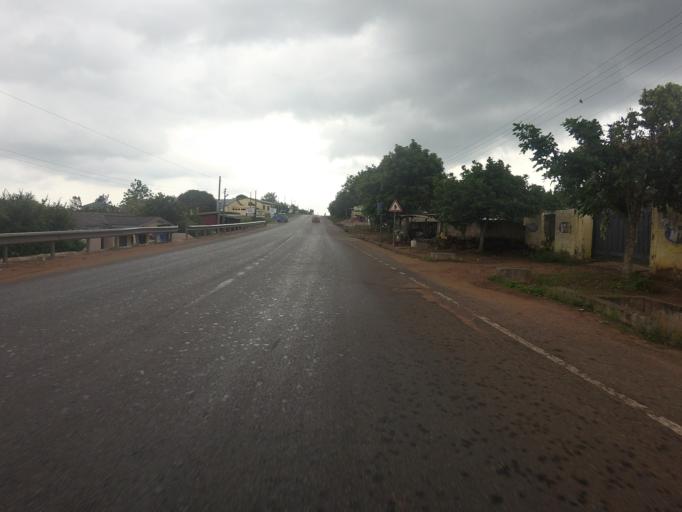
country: GH
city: Akropong
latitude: 5.9316
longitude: -0.1261
